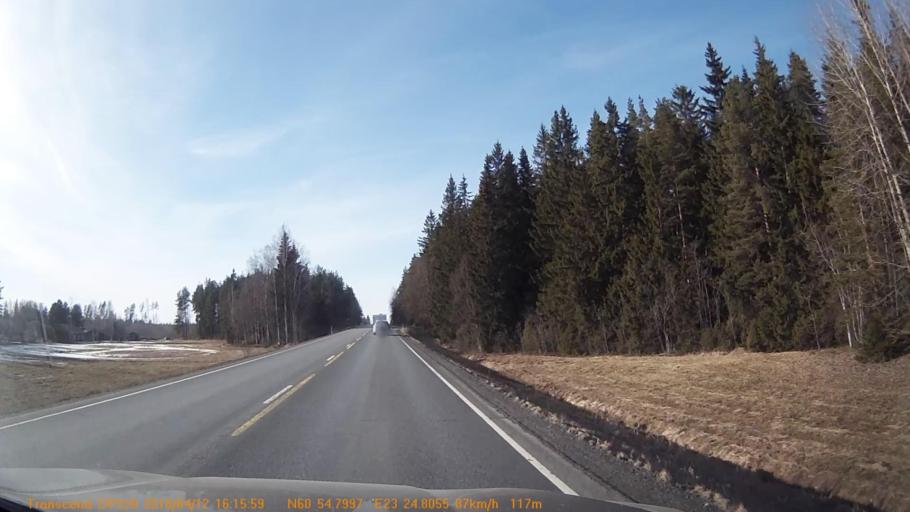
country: FI
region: Haeme
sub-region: Forssa
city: Humppila
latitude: 60.9134
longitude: 23.4133
